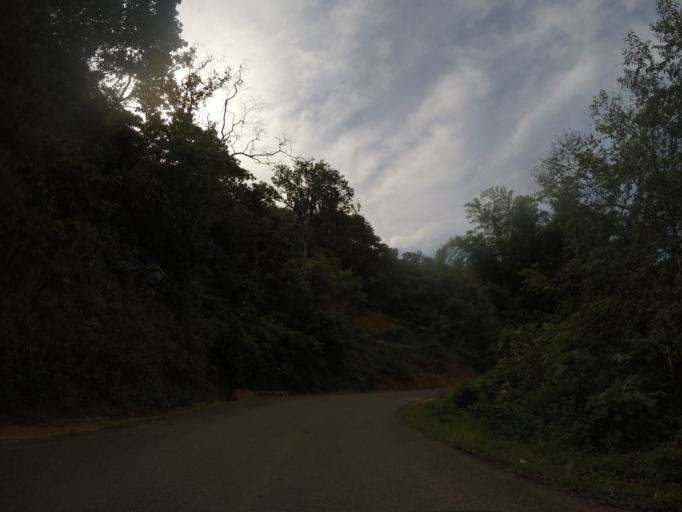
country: MX
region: Oaxaca
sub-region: San Pedro Pochutla
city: Los Naranjos Esquipulas
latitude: 15.9608
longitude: -96.4566
